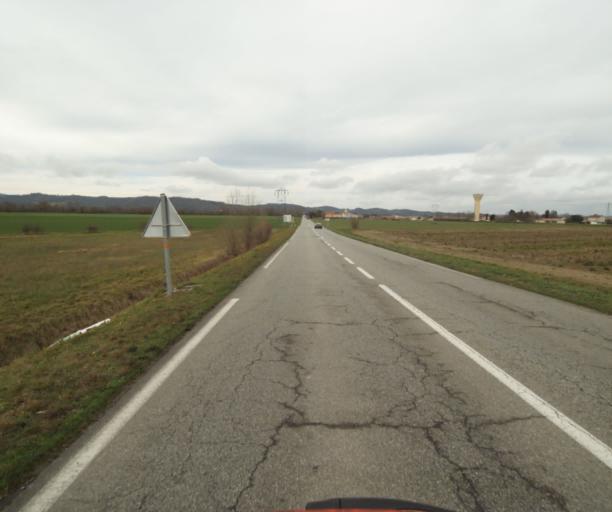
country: FR
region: Midi-Pyrenees
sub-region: Departement de l'Ariege
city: La Tour-du-Crieu
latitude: 43.0981
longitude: 1.6527
